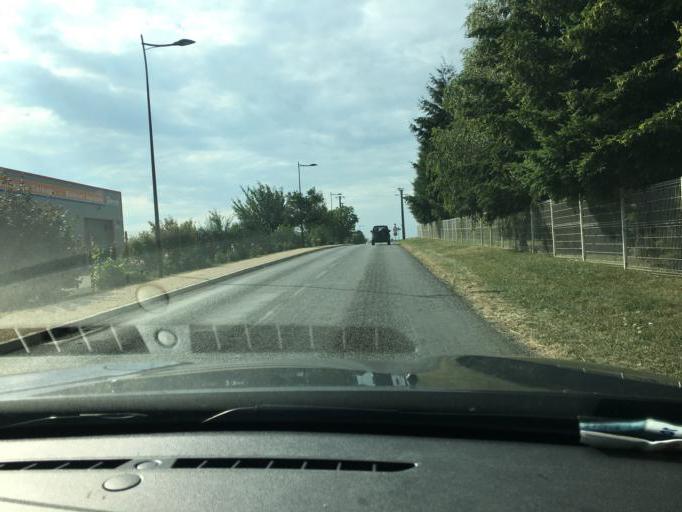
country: FR
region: Centre
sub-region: Departement du Cher
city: Rians
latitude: 47.1904
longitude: 2.6059
